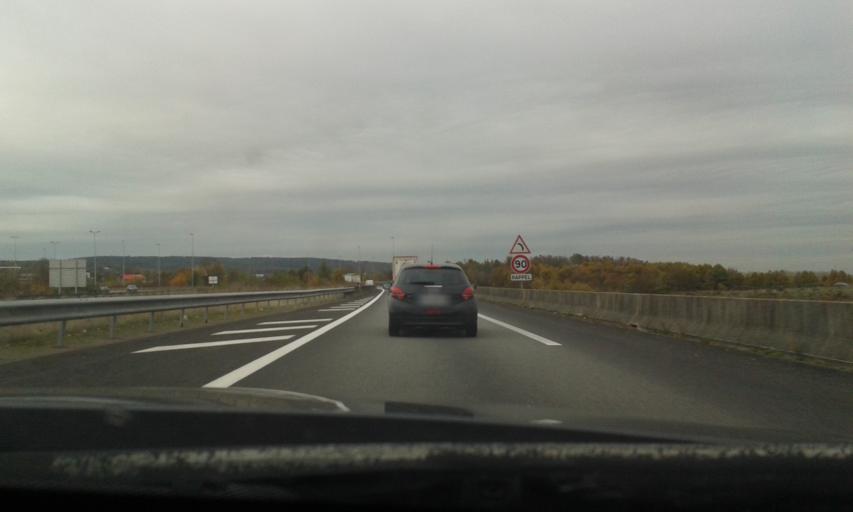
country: FR
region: Haute-Normandie
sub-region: Departement de l'Eure
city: Le Vaudreuil
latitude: 49.2430
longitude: 1.1863
